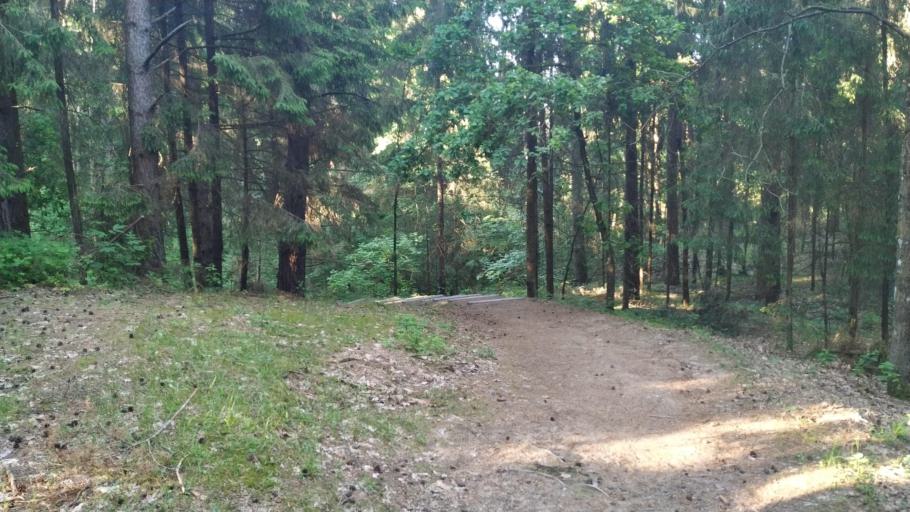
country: LT
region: Utenos apskritis
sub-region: Anyksciai
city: Anyksciai
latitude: 55.5082
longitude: 25.0718
